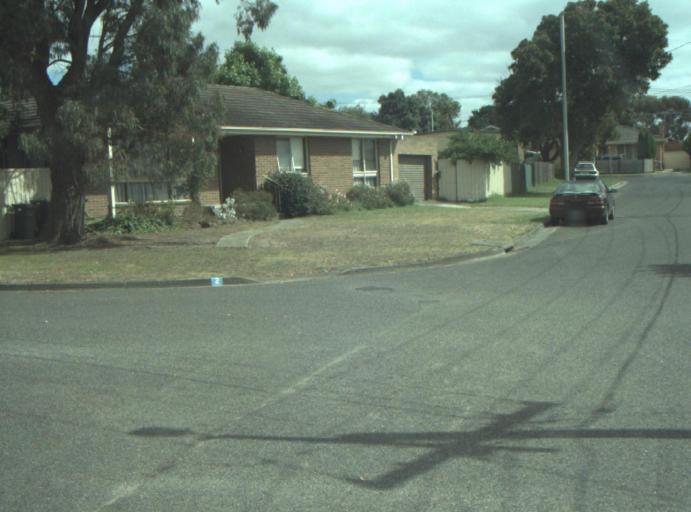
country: AU
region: Victoria
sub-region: Greater Geelong
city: Wandana Heights
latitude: -38.2109
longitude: 144.3335
